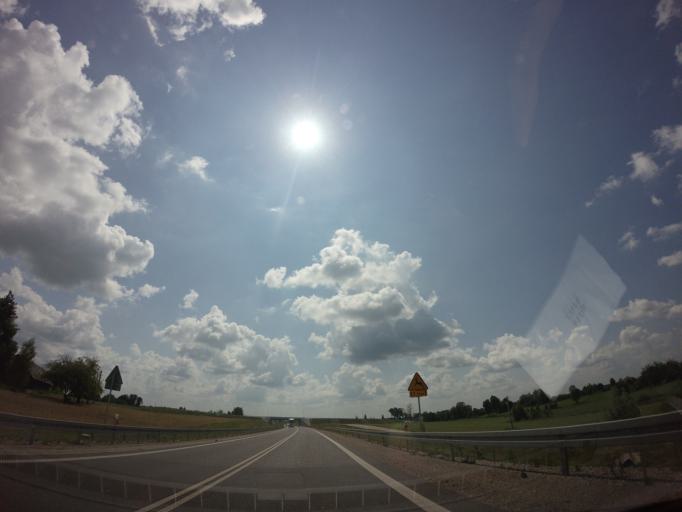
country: PL
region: Podlasie
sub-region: Powiat grajewski
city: Rajgrod
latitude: 53.7760
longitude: 22.8363
